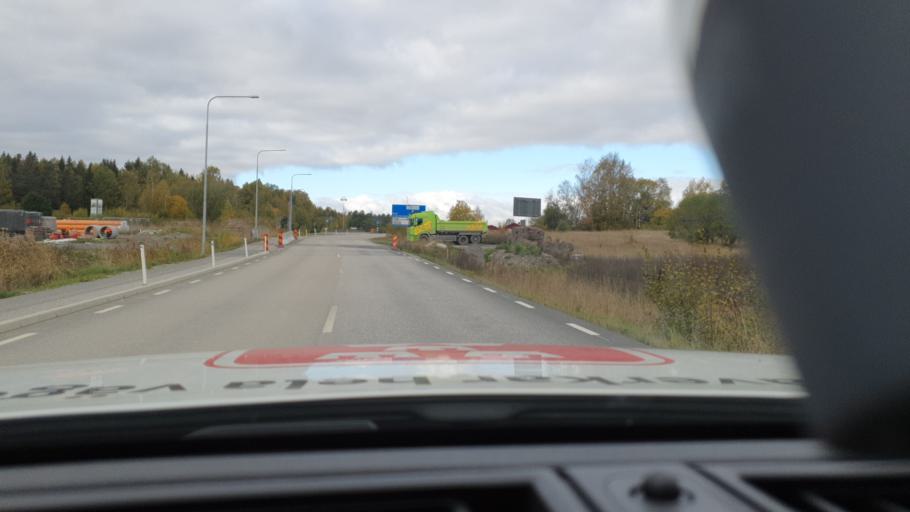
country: SE
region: Stockholm
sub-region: Upplands-Bro Kommun
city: Bro
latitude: 59.5128
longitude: 17.6187
